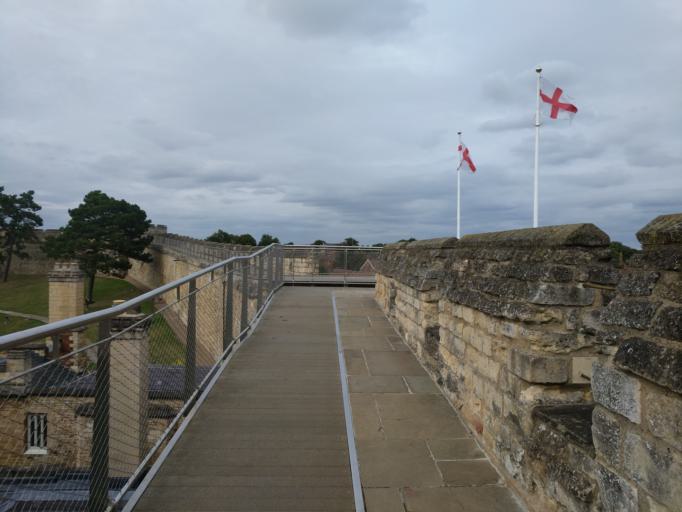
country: GB
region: England
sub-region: Lincolnshire
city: Lincoln
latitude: 53.2345
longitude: -0.5399
